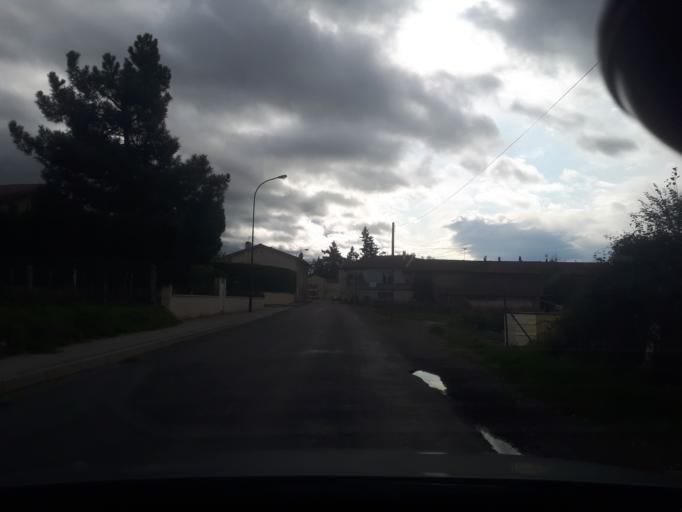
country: FR
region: Rhone-Alpes
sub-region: Departement de la Loire
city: Bellegarde-en-Forez
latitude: 45.6477
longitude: 4.2947
